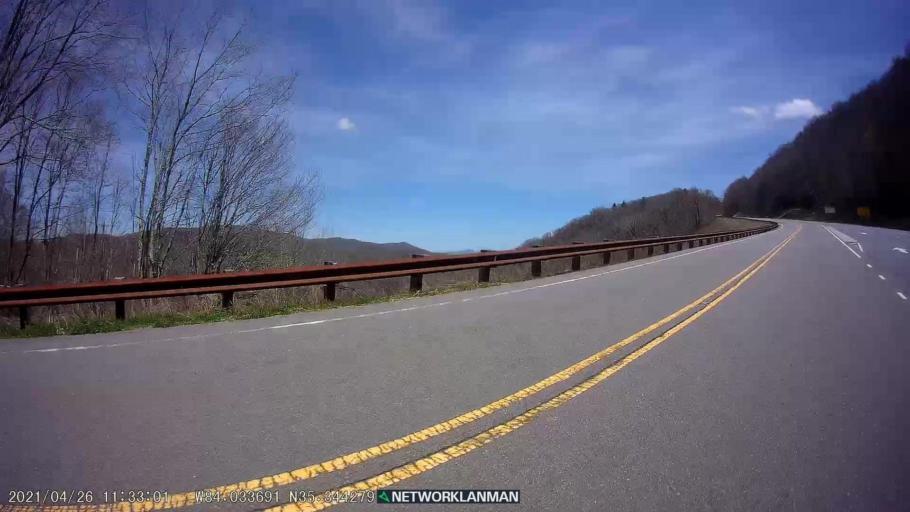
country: US
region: North Carolina
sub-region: Graham County
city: Robbinsville
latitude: 35.3441
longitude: -84.0334
